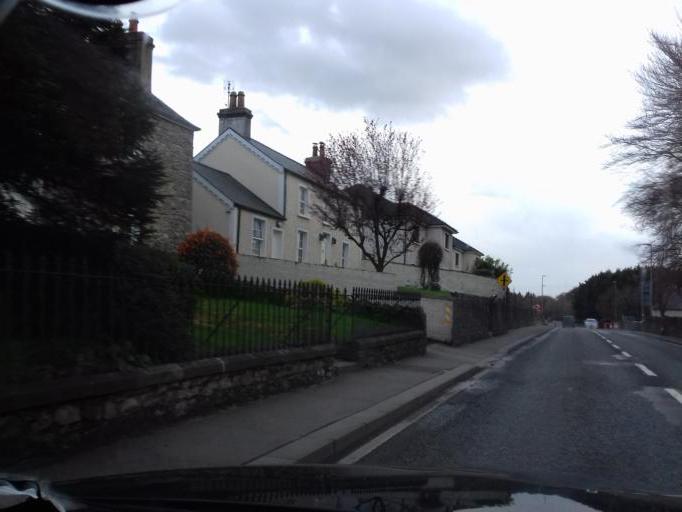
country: IE
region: Leinster
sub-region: Laois
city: Abbeyleix
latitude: 52.9102
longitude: -7.3512
